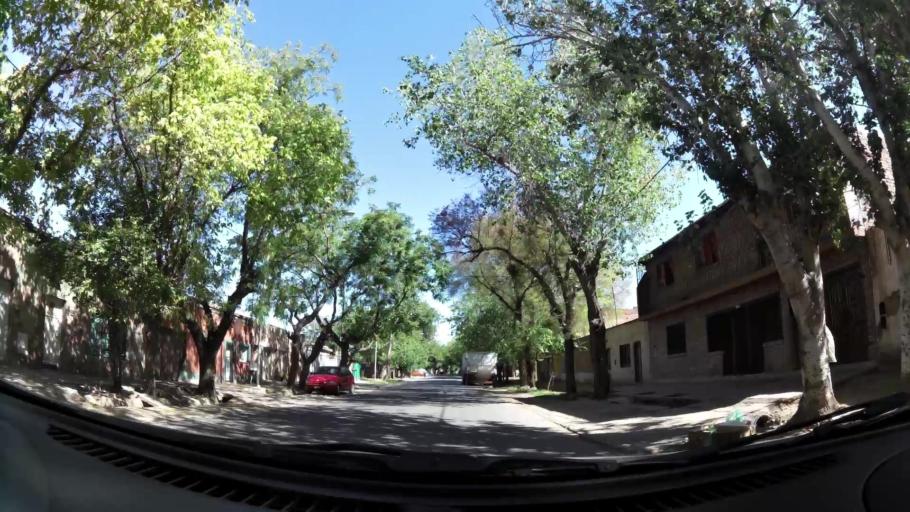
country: AR
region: Mendoza
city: Mendoza
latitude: -32.8814
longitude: -68.8116
